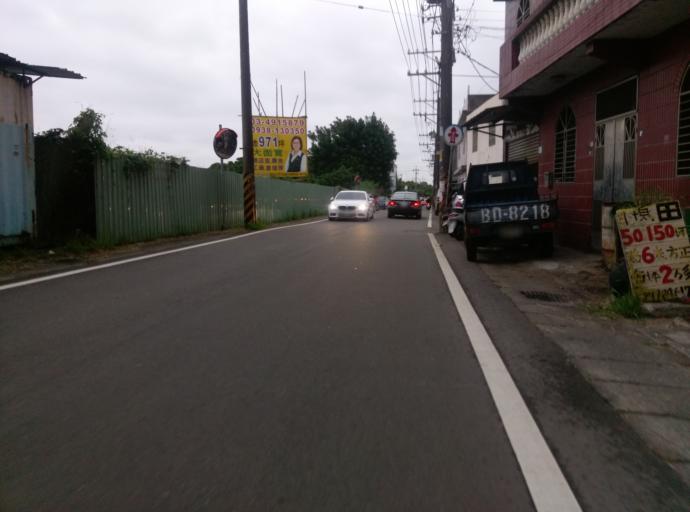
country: TW
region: Taiwan
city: Daxi
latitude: 24.9150
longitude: 121.2382
